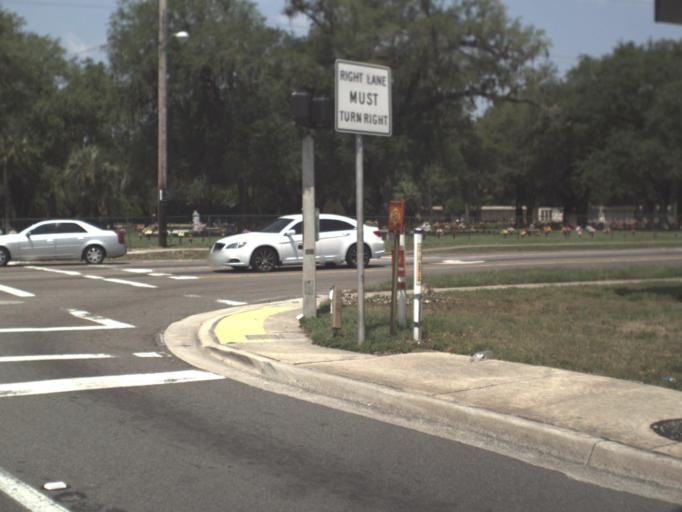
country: US
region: Florida
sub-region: Duval County
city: Jacksonville
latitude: 30.2996
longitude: -81.7671
